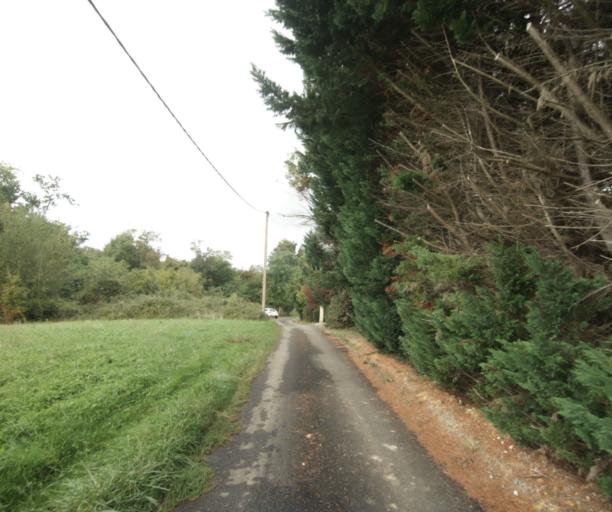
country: FR
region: Midi-Pyrenees
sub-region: Departement du Gers
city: Nogaro
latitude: 43.8166
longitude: -0.0775
